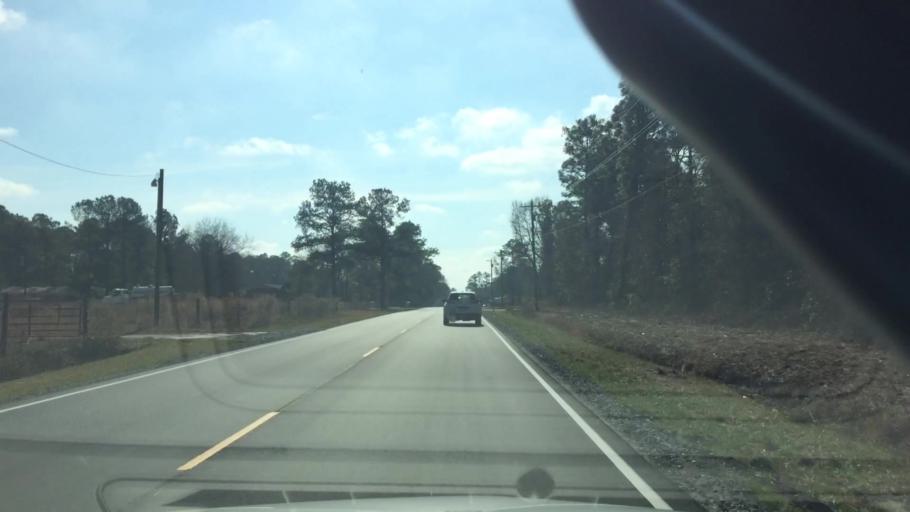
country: US
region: North Carolina
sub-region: Duplin County
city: Beulaville
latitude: 34.9846
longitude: -77.7589
